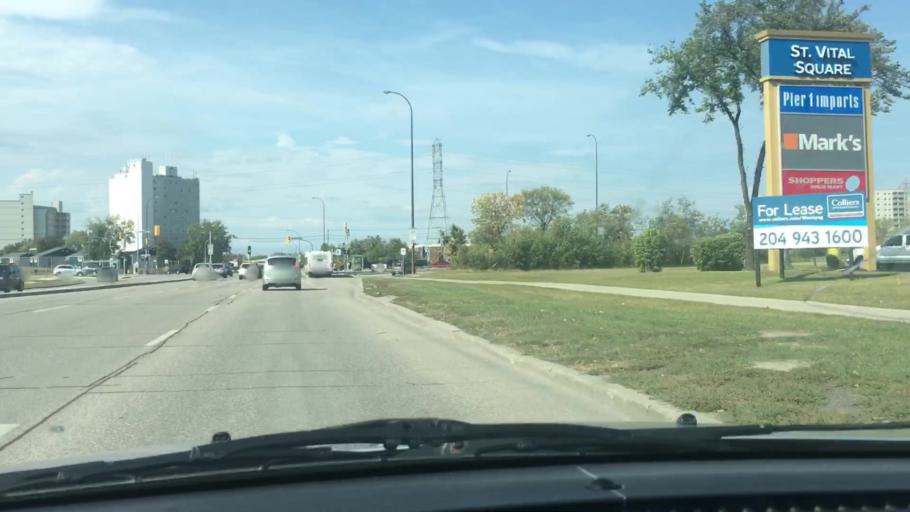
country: CA
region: Manitoba
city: Winnipeg
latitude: 49.8315
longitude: -97.1077
